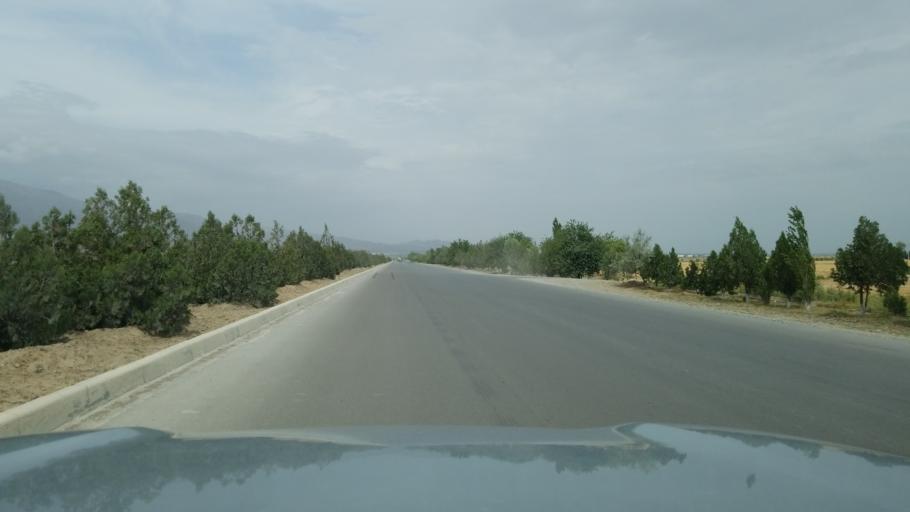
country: TM
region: Ahal
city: Arcabil
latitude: 38.1754
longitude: 57.8962
